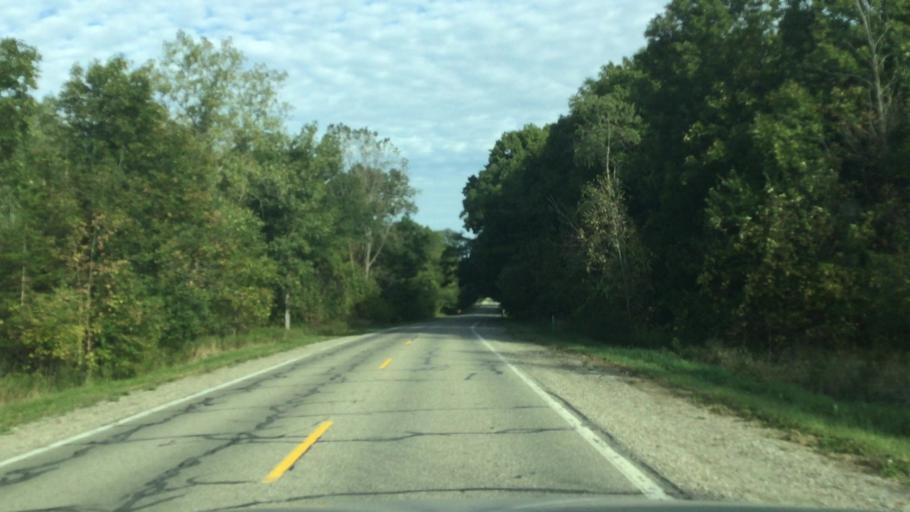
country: US
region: Michigan
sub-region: Livingston County
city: Howell
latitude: 42.5476
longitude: -83.8797
